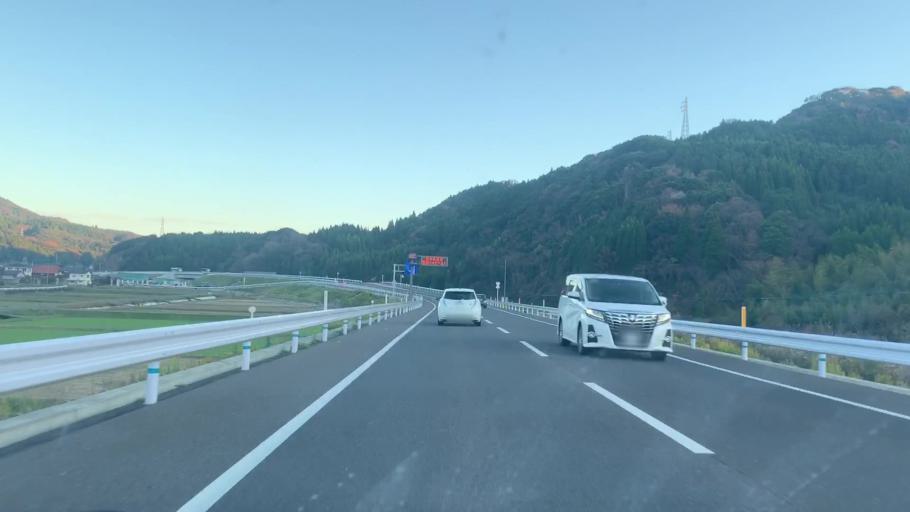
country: JP
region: Saga Prefecture
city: Takeocho-takeo
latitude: 33.2521
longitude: 129.9904
